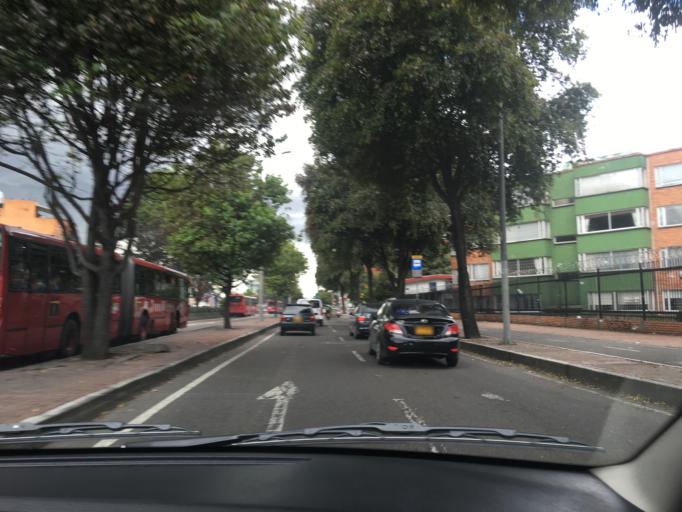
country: CO
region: Bogota D.C.
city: Barrio San Luis
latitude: 4.6678
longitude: -74.0622
